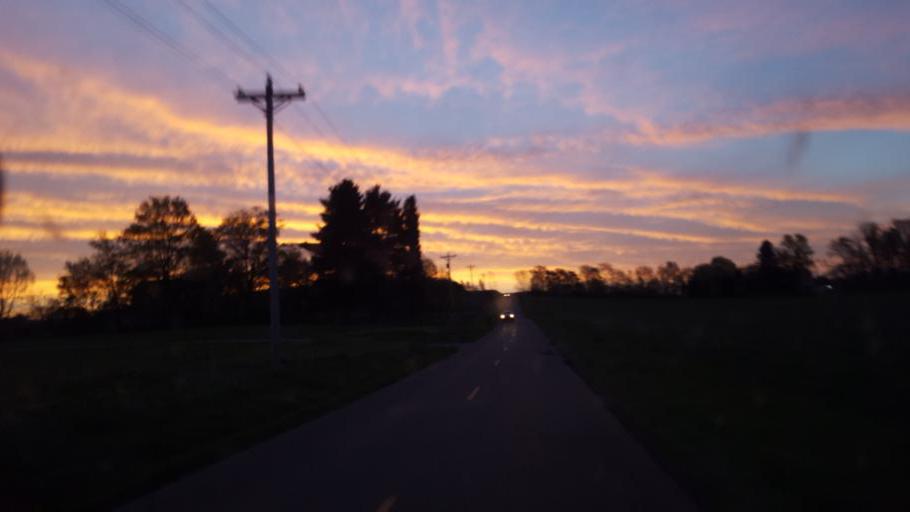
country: US
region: Ohio
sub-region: Knox County
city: Fredericktown
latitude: 40.4732
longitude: -82.4768
